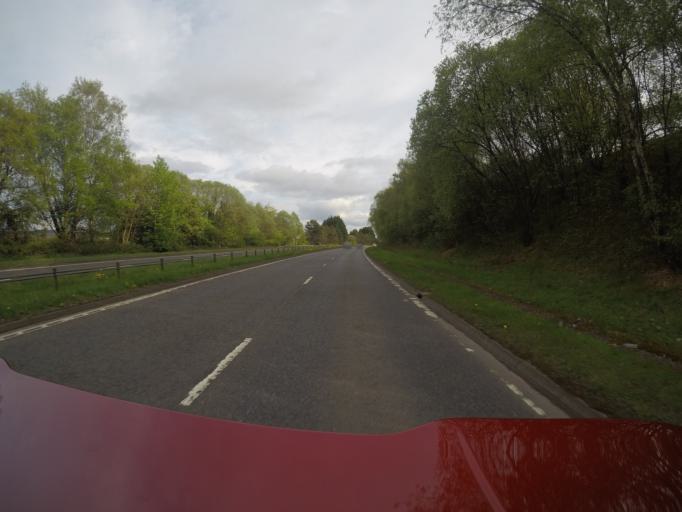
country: GB
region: Scotland
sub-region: West Dunbartonshire
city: Alexandria
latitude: 55.9879
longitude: -4.5891
